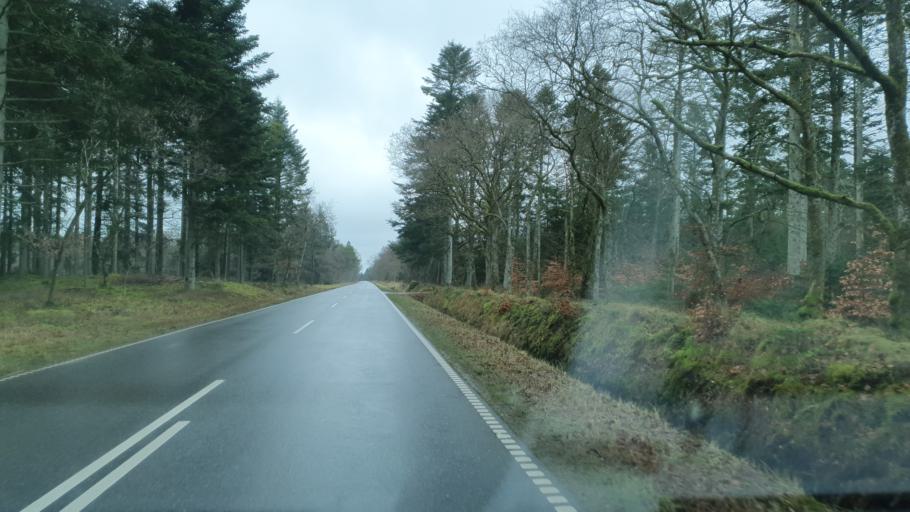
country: DK
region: North Denmark
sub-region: Jammerbugt Kommune
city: Fjerritslev
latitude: 57.1225
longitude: 9.1279
